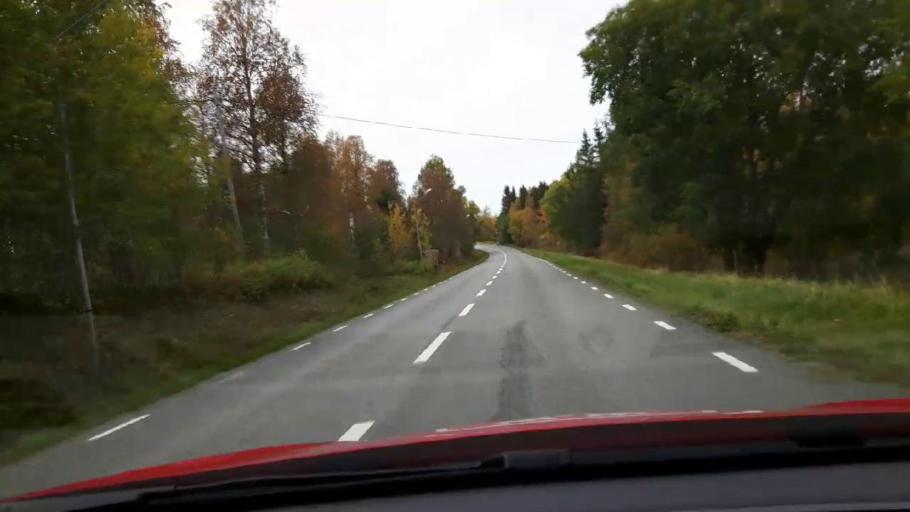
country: SE
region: Jaemtland
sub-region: Krokoms Kommun
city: Krokom
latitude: 63.1792
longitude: 14.0883
